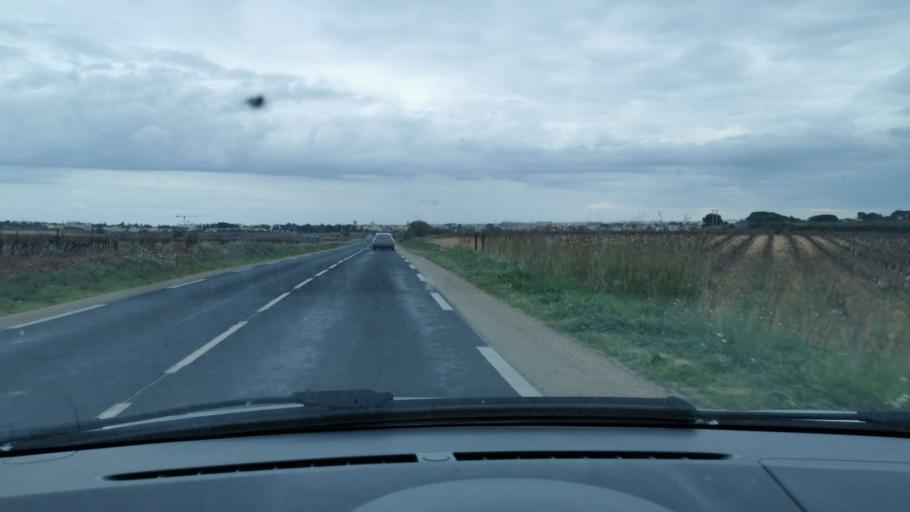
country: FR
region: Languedoc-Roussillon
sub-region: Departement de l'Herault
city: Frontignan
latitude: 43.4480
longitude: 3.7283
